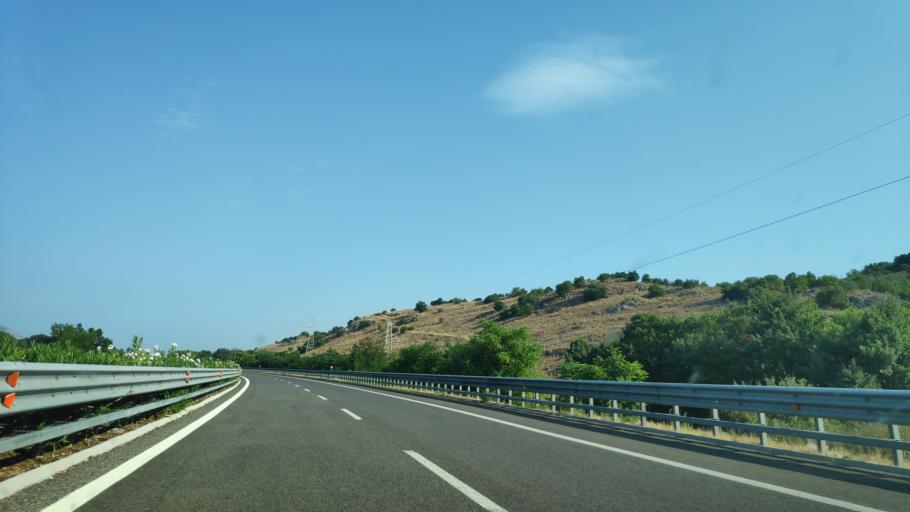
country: IT
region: Campania
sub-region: Provincia di Salerno
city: Atena Lucana
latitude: 40.4364
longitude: 15.5556
